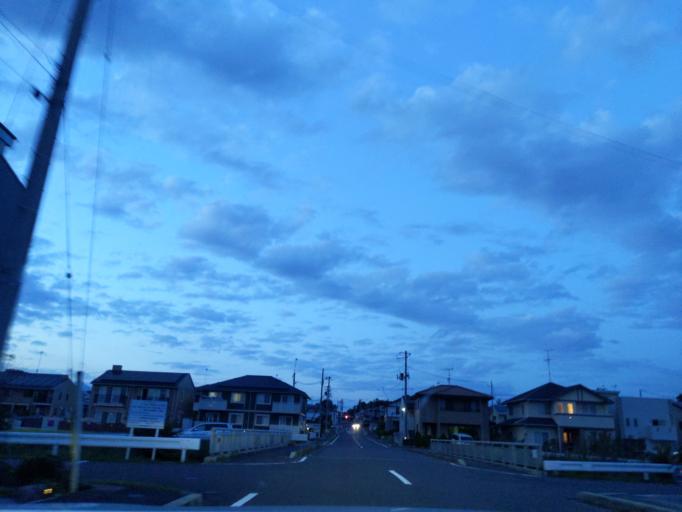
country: JP
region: Fukushima
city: Koriyama
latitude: 37.4221
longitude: 140.3387
